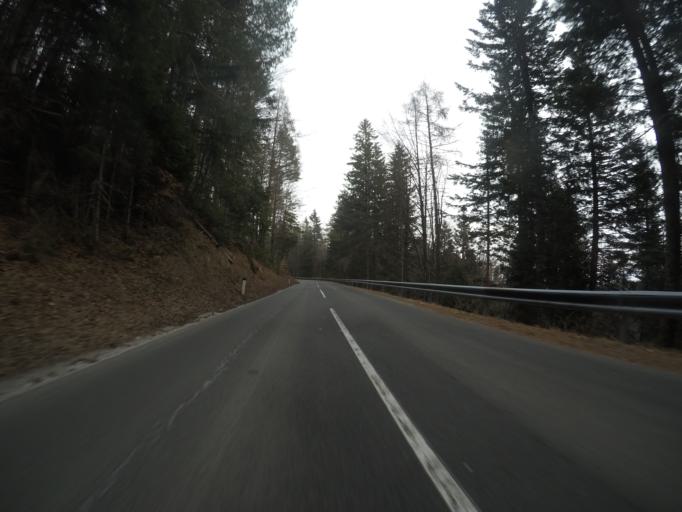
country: SI
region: Ruse
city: Ruse
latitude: 46.4920
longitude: 15.5395
